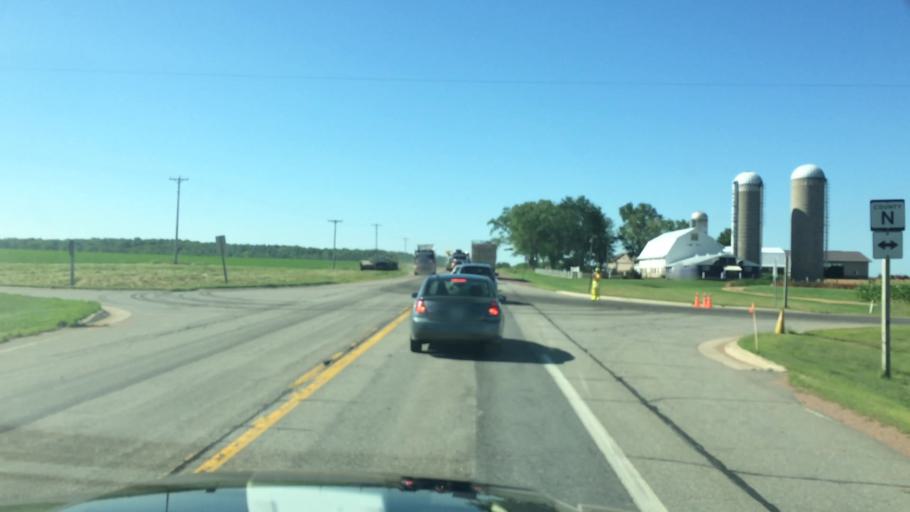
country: US
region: Wisconsin
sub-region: Marathon County
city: Stratford
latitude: 44.9024
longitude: -90.0787
